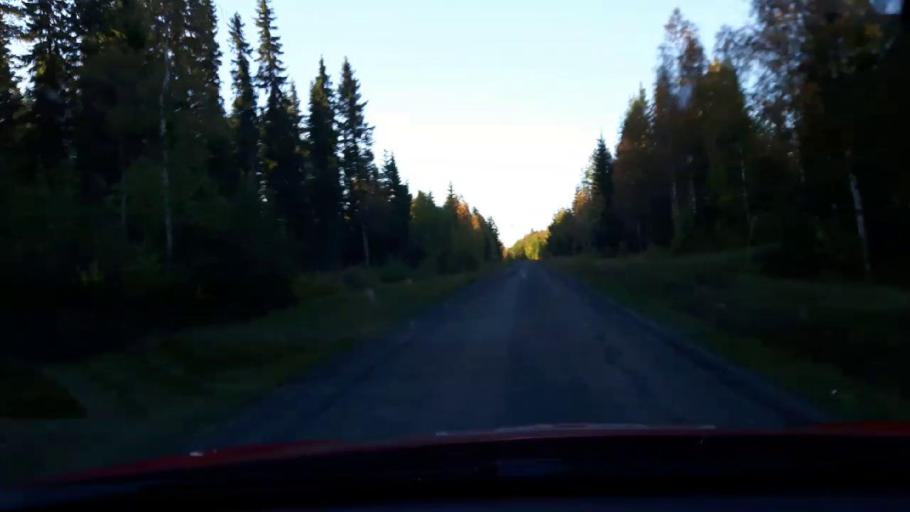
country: SE
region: Jaemtland
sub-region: Krokoms Kommun
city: Krokom
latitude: 63.4338
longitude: 14.6080
